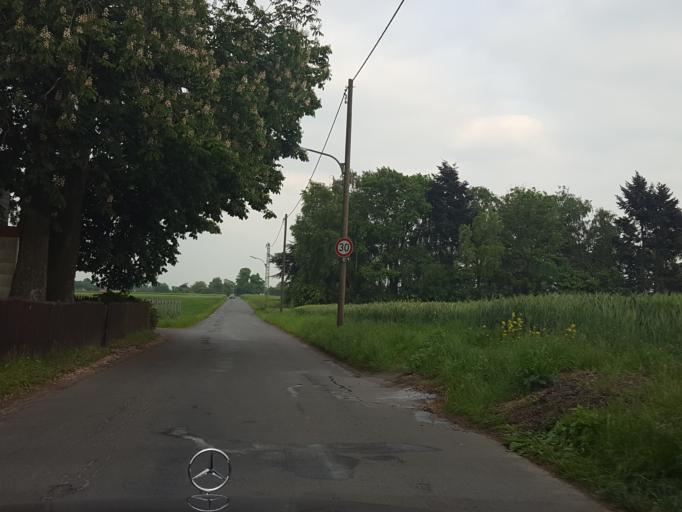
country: DE
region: North Rhine-Westphalia
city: Oer-Erkenschwick
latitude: 51.6178
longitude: 7.2435
